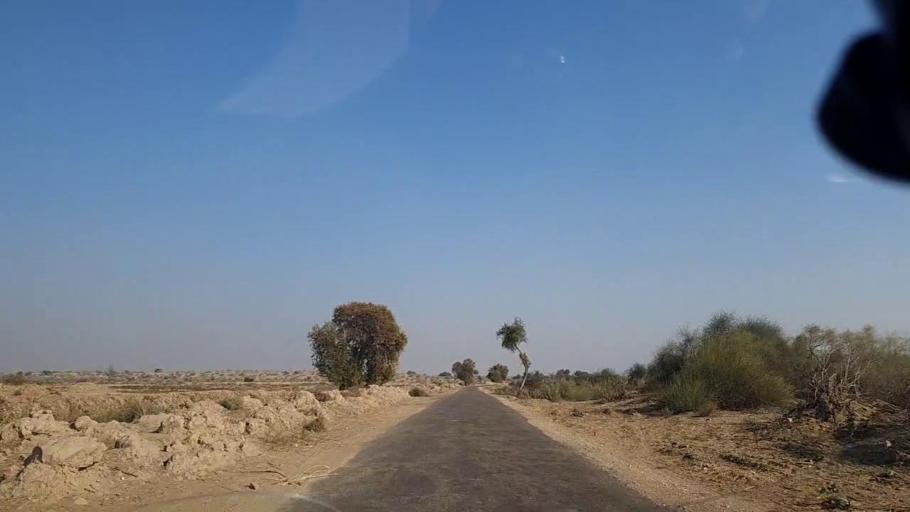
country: PK
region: Sindh
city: Khanpur
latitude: 27.6820
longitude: 69.5509
